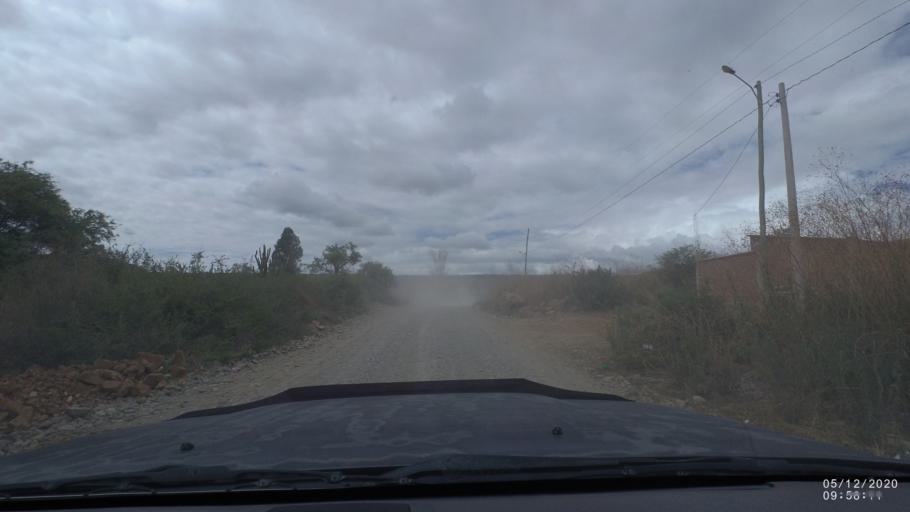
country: BO
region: Cochabamba
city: Sipe Sipe
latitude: -17.4280
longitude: -66.2910
